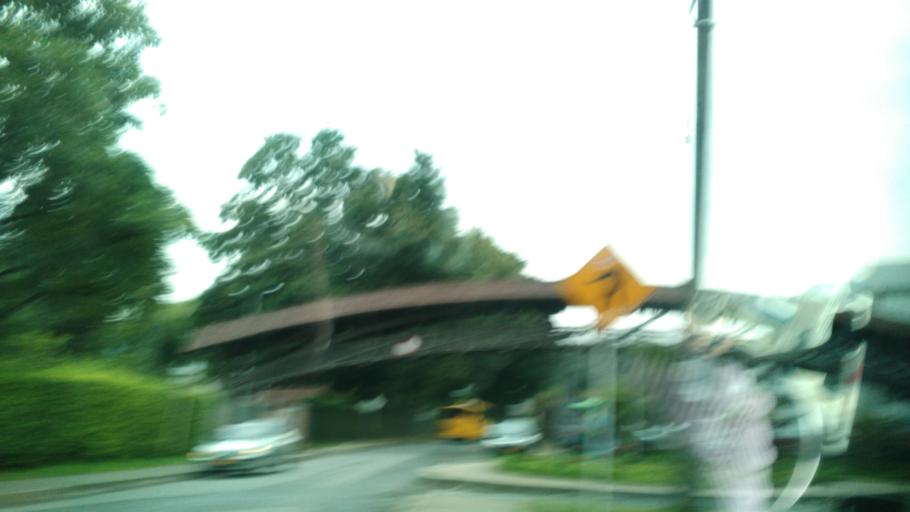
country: CO
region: Risaralda
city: Pereira
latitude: 4.7915
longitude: -75.6900
